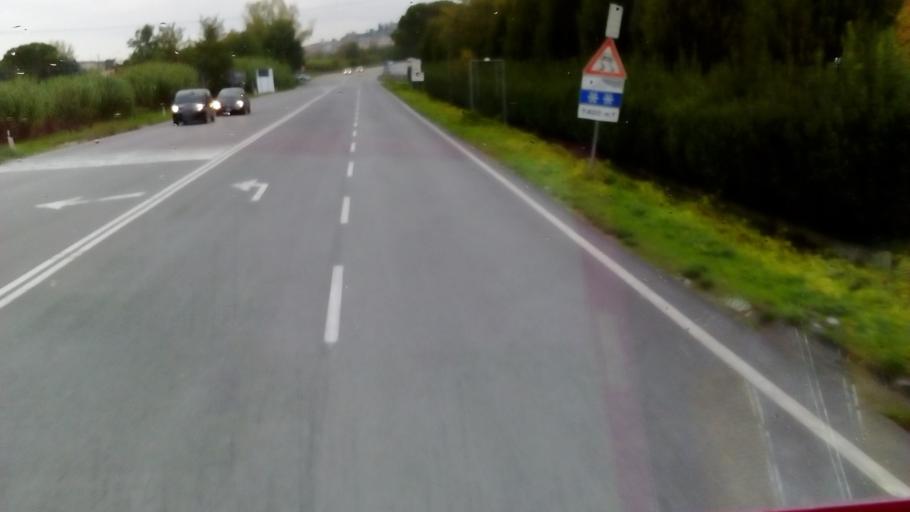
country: IT
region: Tuscany
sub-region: Province of Florence
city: Castelfiorentino
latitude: 43.5935
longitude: 10.9723
